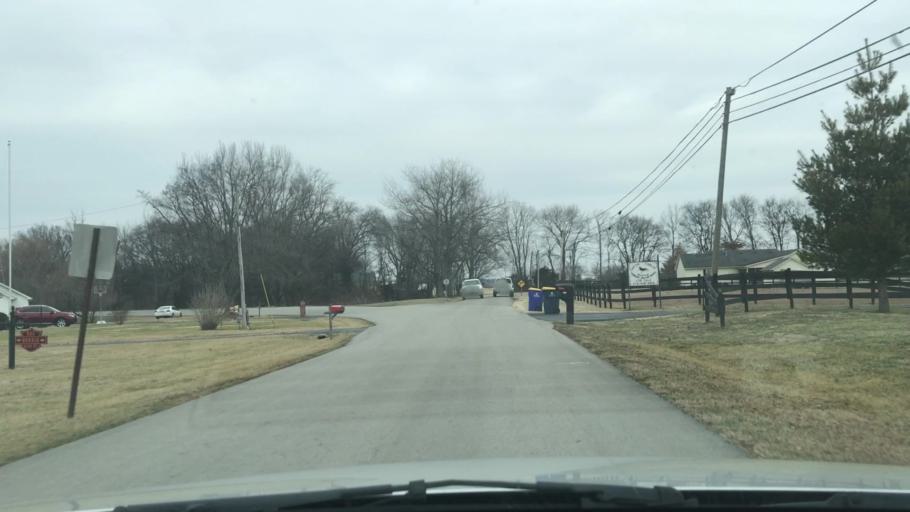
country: US
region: Kentucky
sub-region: Edmonson County
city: Brownsville
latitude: 37.0460
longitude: -86.2509
